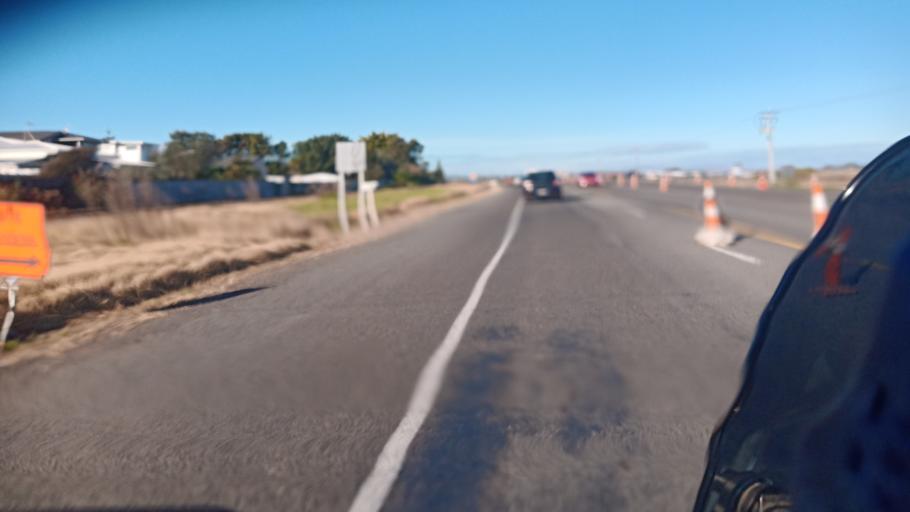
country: NZ
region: Hawke's Bay
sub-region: Napier City
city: Napier
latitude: -39.4593
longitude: 176.8726
